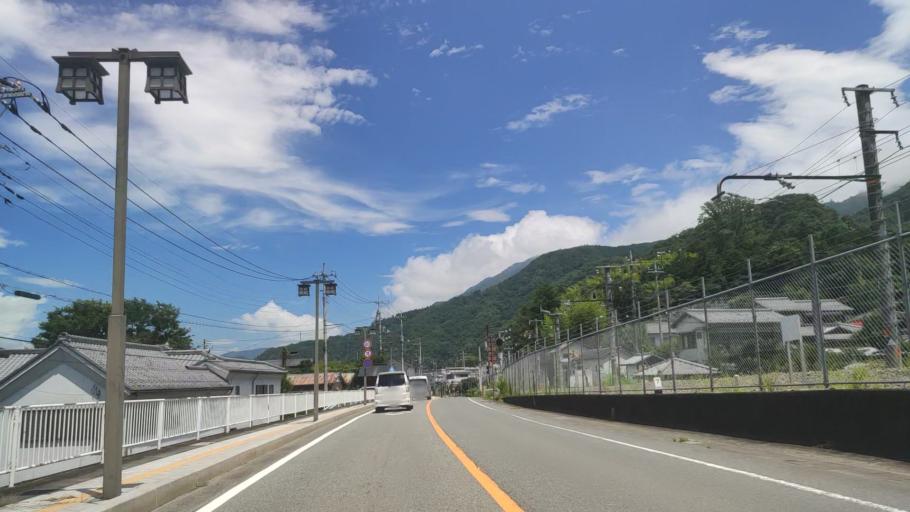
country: JP
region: Shizuoka
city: Fujinomiya
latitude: 35.3573
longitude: 138.4512
